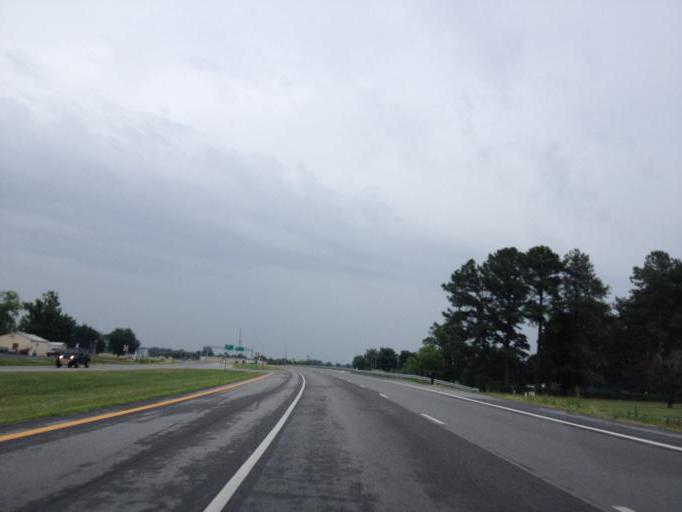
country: US
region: Maryland
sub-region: Caroline County
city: Denton
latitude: 38.8980
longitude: -75.8597
